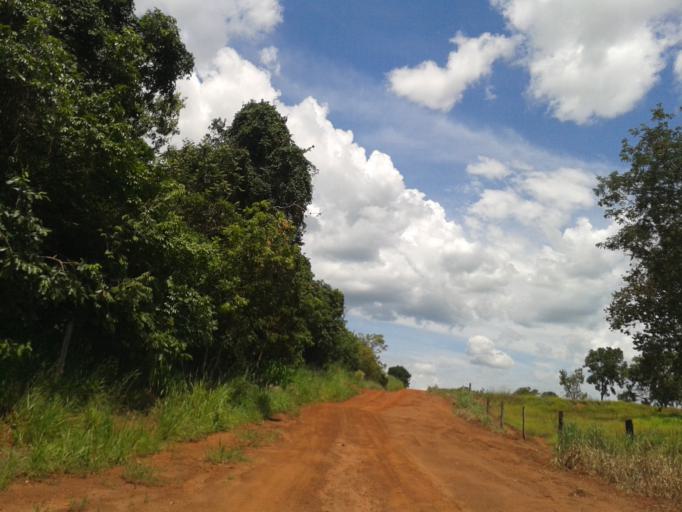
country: BR
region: Minas Gerais
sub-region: Ituiutaba
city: Ituiutaba
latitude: -18.8697
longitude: -49.4893
